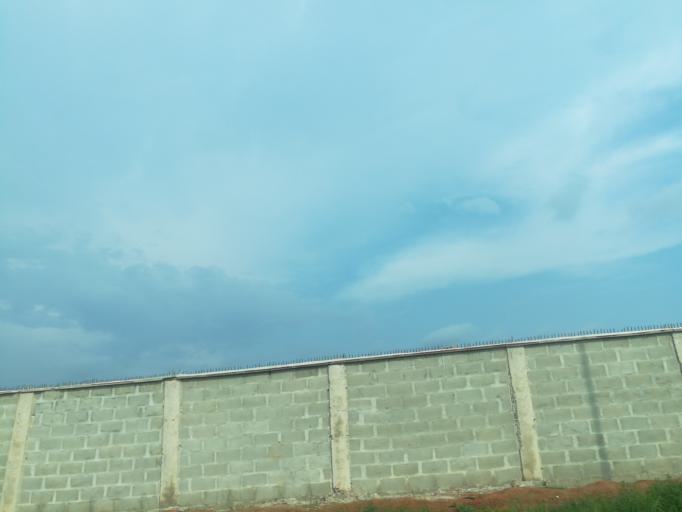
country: NG
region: Lagos
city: Ikorodu
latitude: 6.6617
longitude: 3.6699
